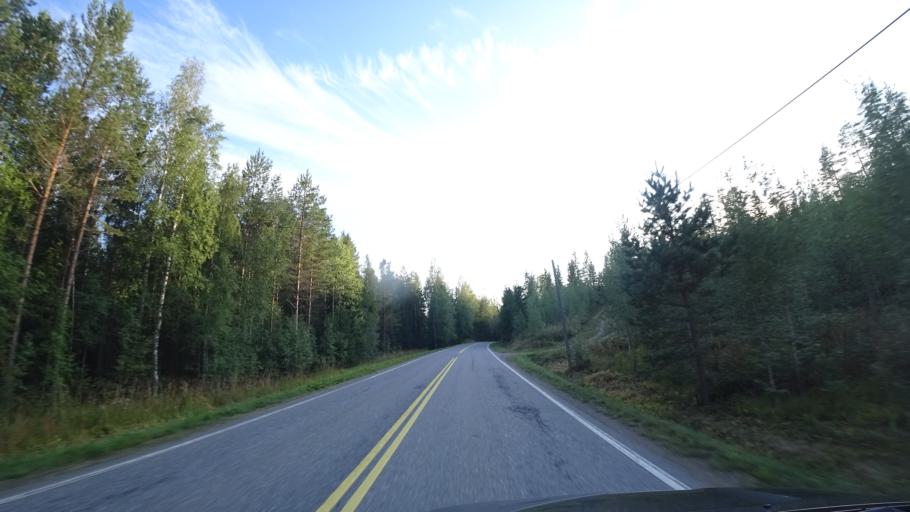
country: FI
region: Haeme
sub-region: Haemeenlinna
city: Lammi
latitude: 61.0529
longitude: 24.9614
